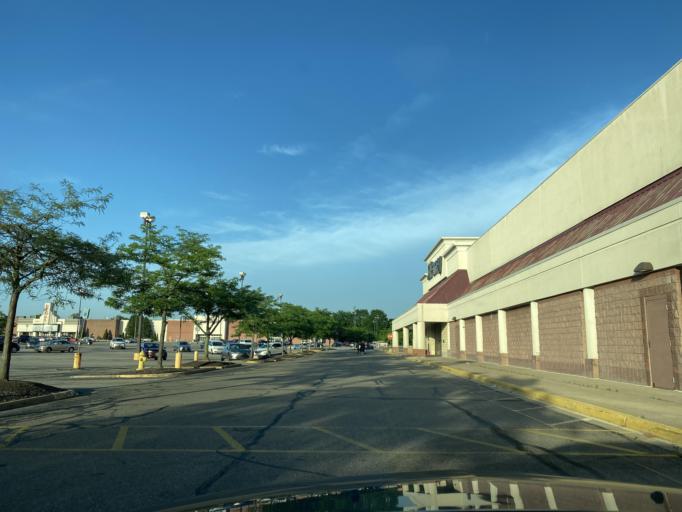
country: US
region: Ohio
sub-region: Summit County
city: Montrose-Ghent
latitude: 41.1317
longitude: -81.6448
